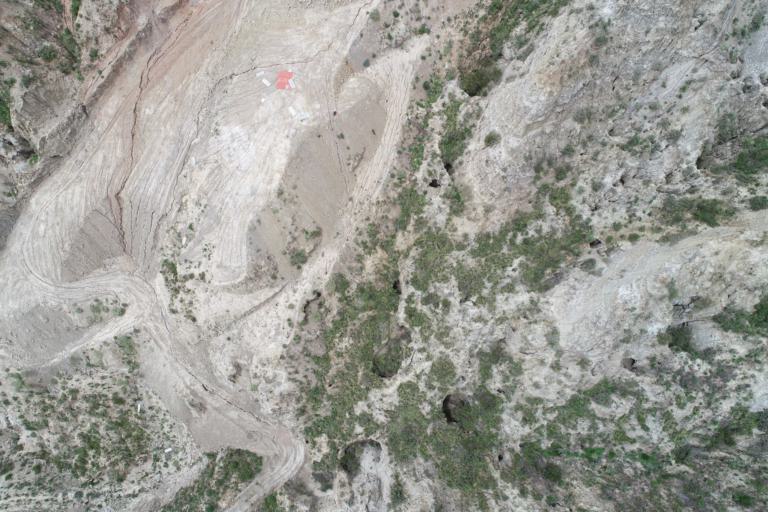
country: BO
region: La Paz
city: La Paz
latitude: -16.5439
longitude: -68.1183
